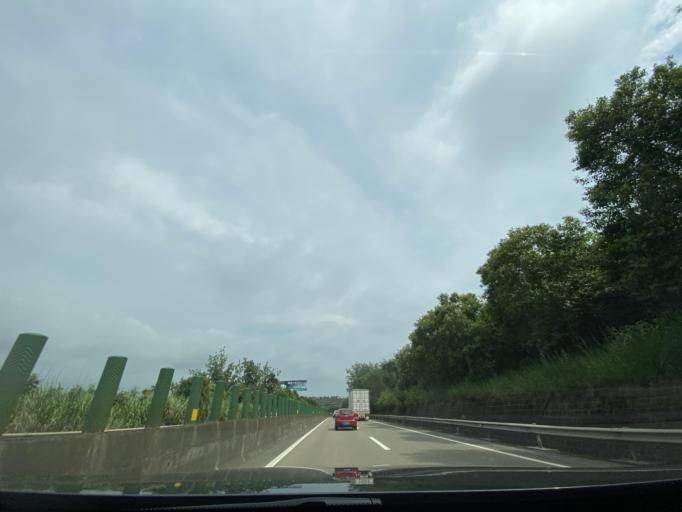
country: CN
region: Sichuan
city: Chonglong
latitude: 29.7178
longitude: 104.9384
